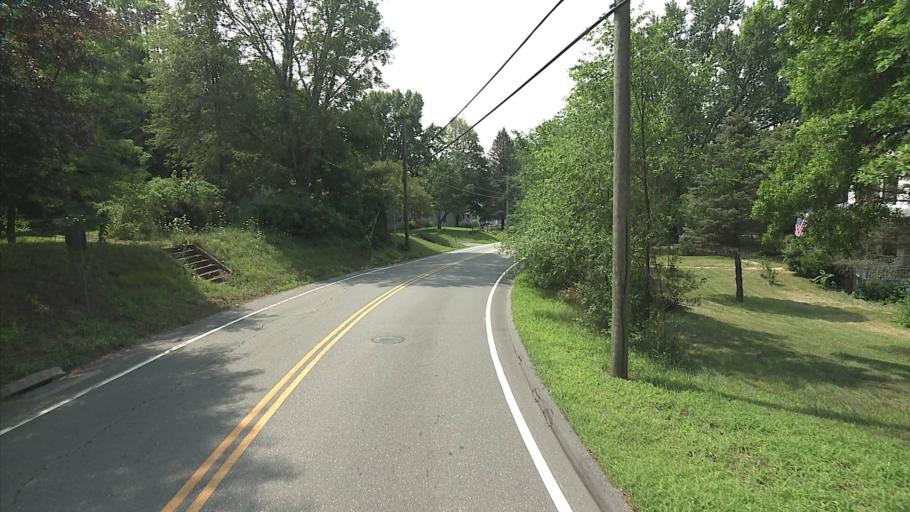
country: US
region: Connecticut
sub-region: Windham County
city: Moosup
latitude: 41.7229
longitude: -71.8694
